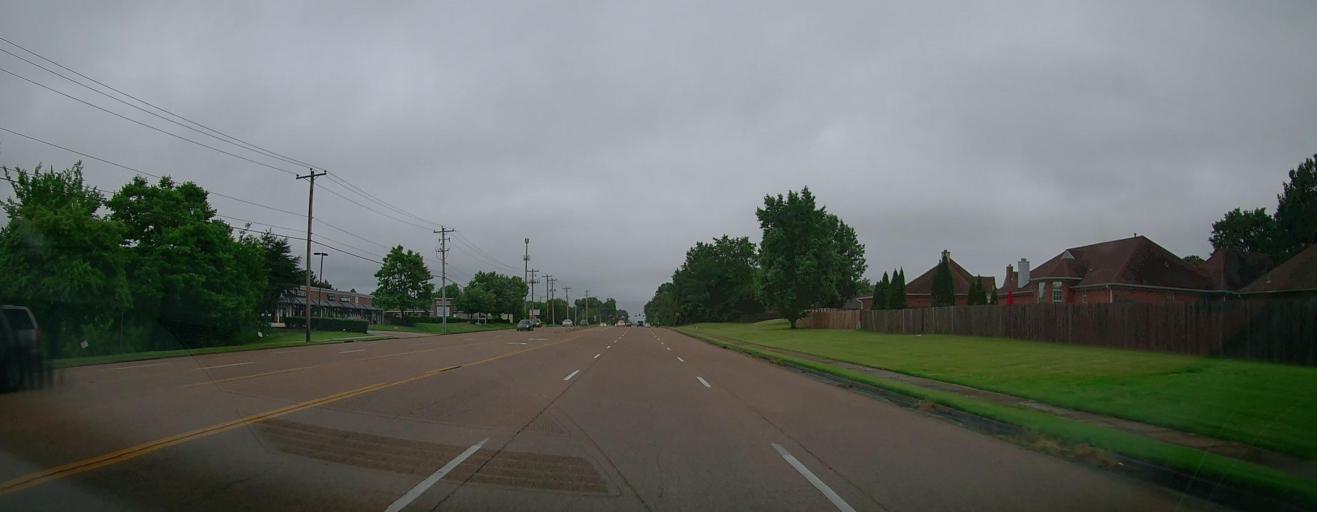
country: US
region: Mississippi
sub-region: De Soto County
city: Olive Branch
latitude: 35.0090
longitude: -89.8312
